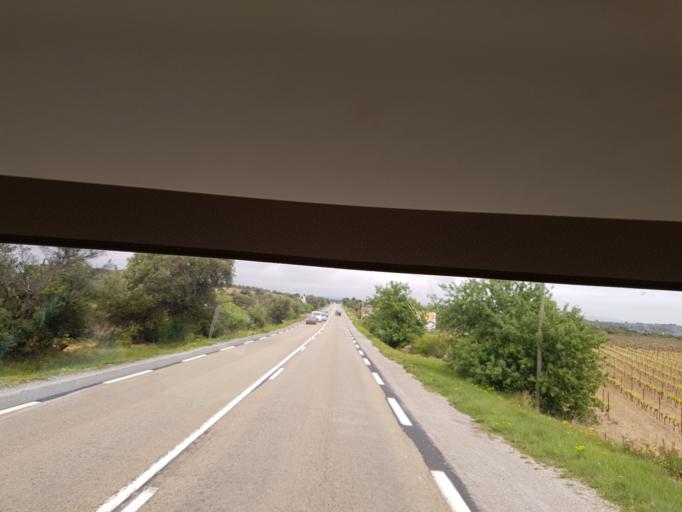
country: FR
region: Languedoc-Roussillon
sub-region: Departement de l'Aude
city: Leucate
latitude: 42.9083
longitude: 2.9995
